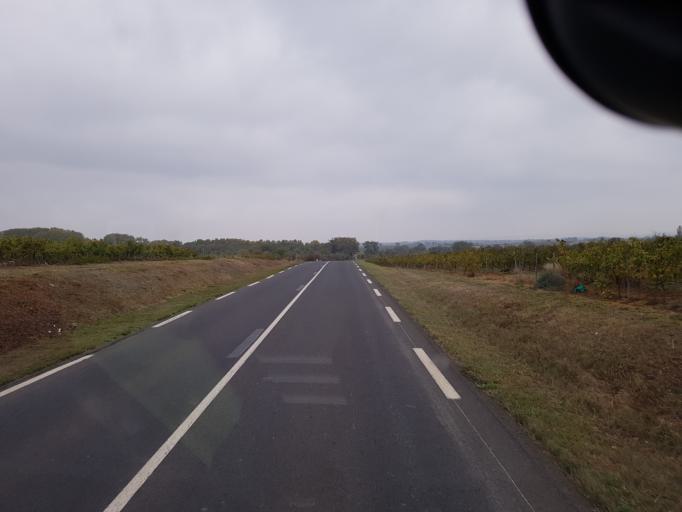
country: FR
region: Languedoc-Roussillon
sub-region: Departement de l'Herault
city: Pinet
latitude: 43.3994
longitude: 3.5390
